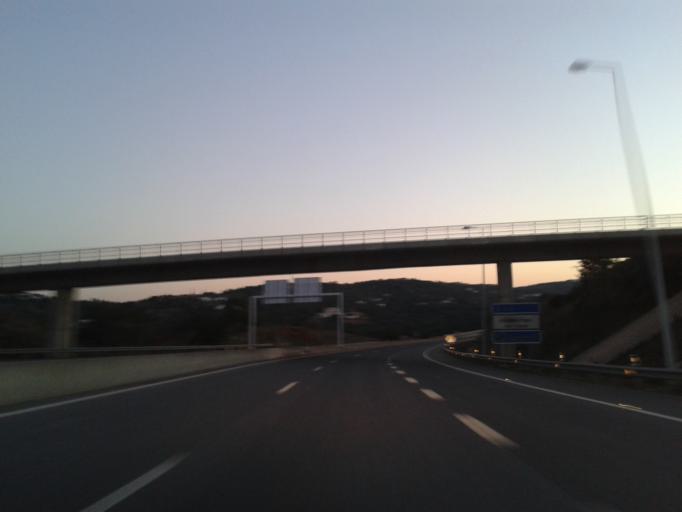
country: PT
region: Faro
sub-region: Albufeira
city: Ferreiras
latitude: 37.1577
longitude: -8.2057
